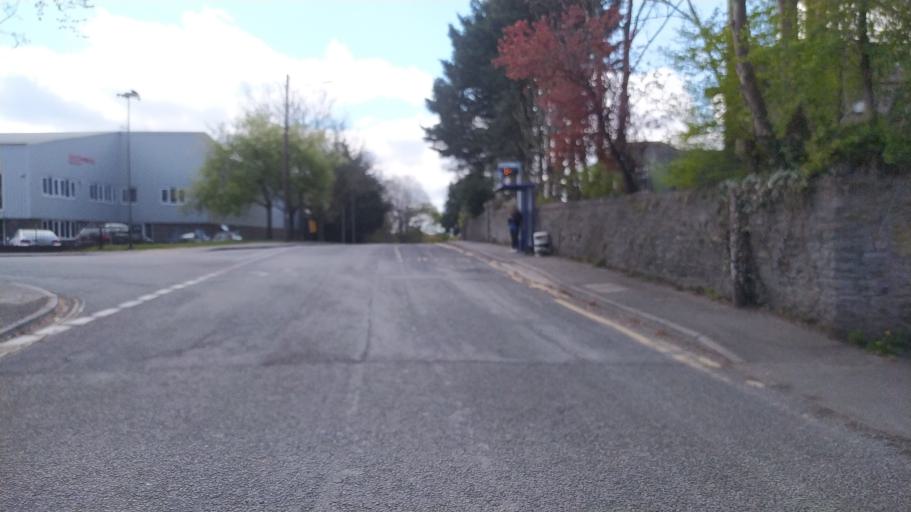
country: GB
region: England
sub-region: South Gloucestershire
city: Siston
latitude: 51.4544
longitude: -2.4757
